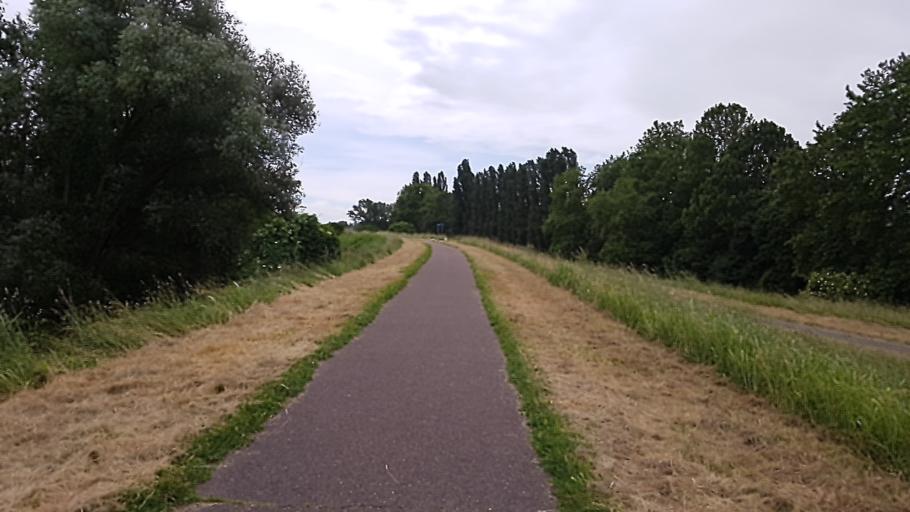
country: IT
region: Veneto
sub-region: Provincia di Verona
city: Angiari
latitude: 45.2108
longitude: 11.2946
